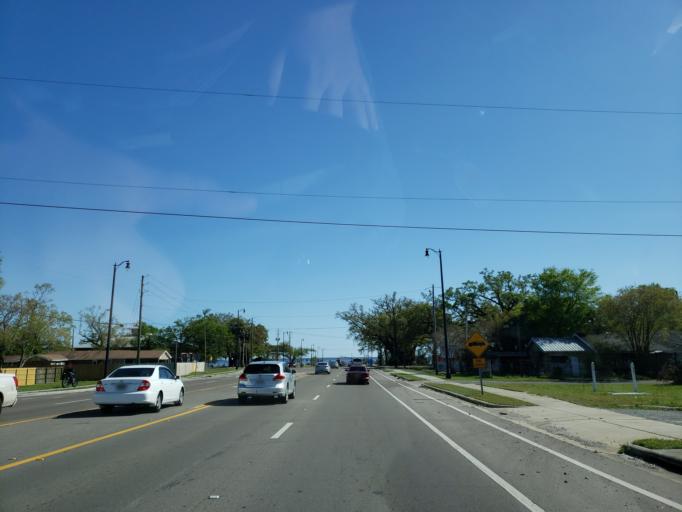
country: US
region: Mississippi
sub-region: Harrison County
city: Gulfport
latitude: 30.3863
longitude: -89.0270
